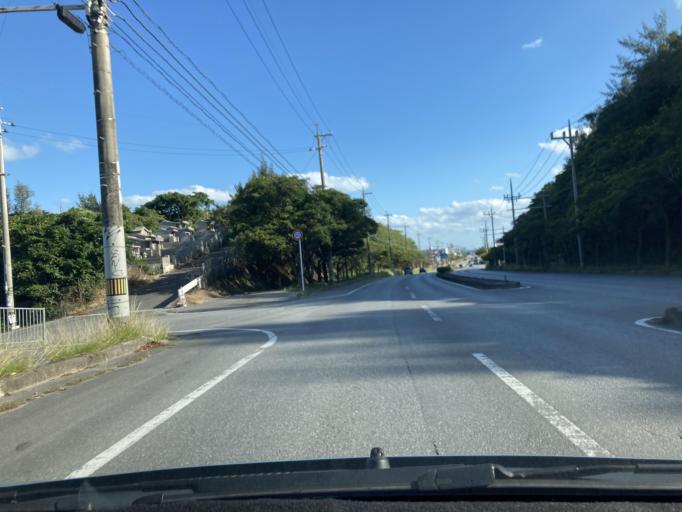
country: JP
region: Okinawa
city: Gushikawa
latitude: 26.3426
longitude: 127.8423
